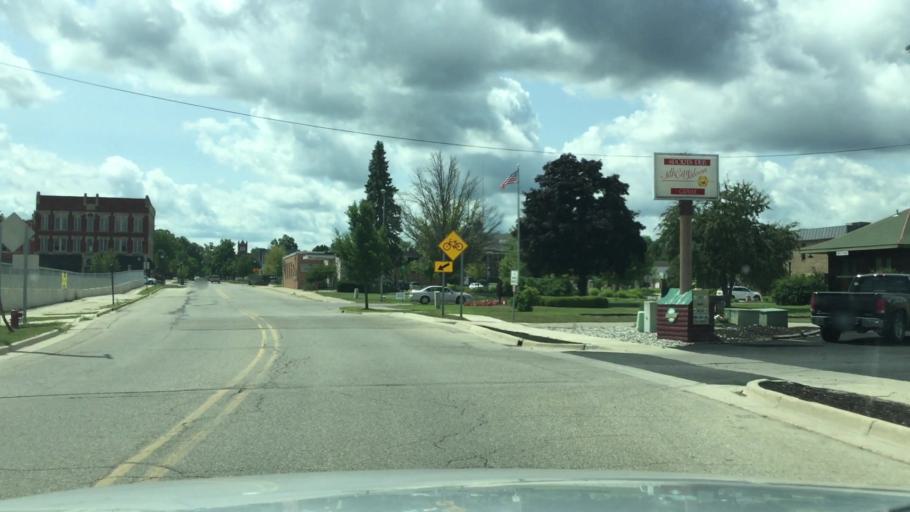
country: US
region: Michigan
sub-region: Ionia County
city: Belding
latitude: 43.0993
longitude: -85.2287
